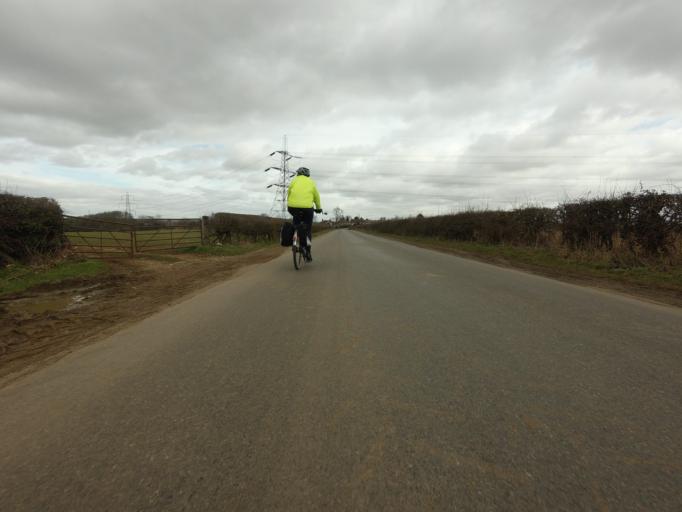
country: GB
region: England
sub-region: Lincolnshire
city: Grantham
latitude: 52.8882
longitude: -0.6605
